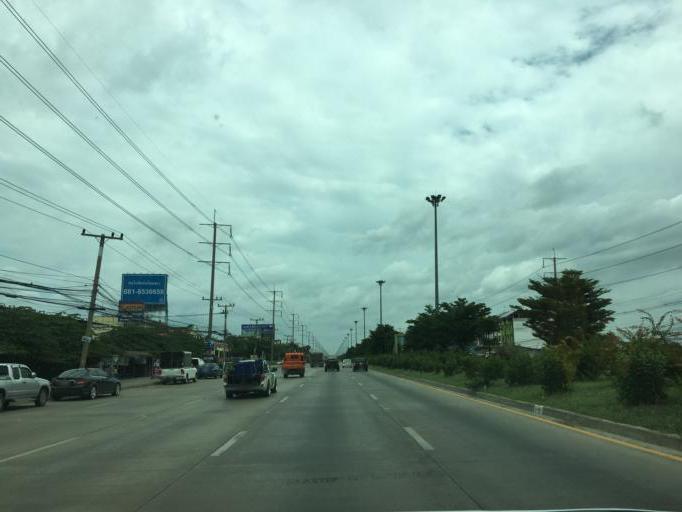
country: TH
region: Phra Nakhon Si Ayutthaya
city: Uthai
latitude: 14.3158
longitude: 100.6379
